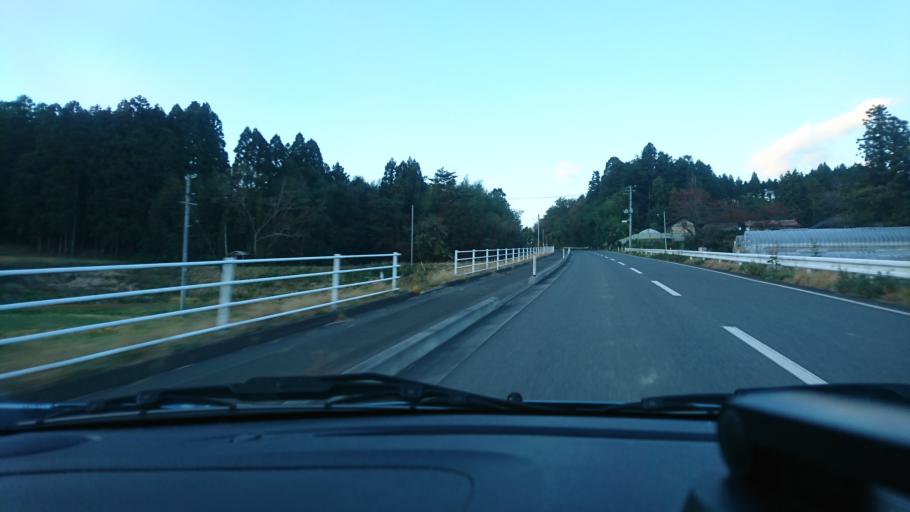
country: JP
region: Iwate
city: Ichinoseki
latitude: 38.7645
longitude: 141.2384
